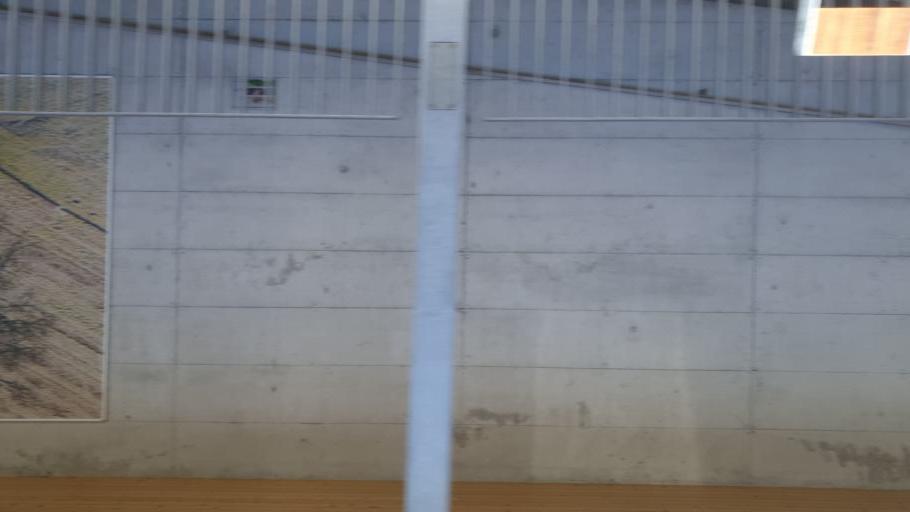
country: CH
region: Fribourg
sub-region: Sarine District
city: Givisiez
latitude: 46.8414
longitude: 7.1346
